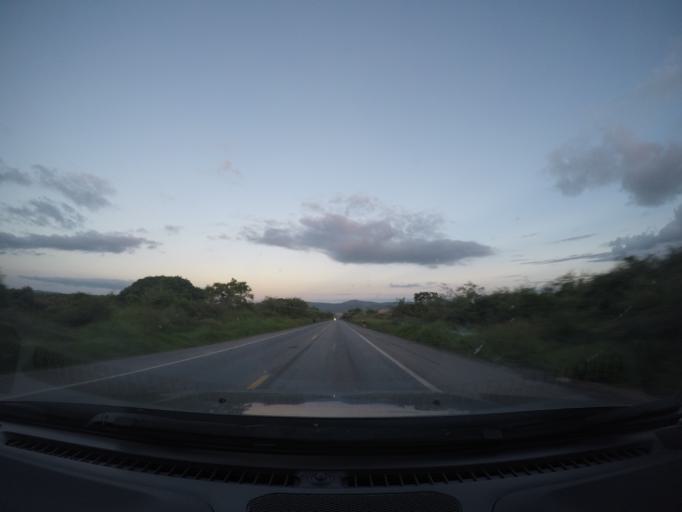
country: BR
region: Bahia
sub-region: Seabra
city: Seabra
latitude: -12.4308
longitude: -41.7956
